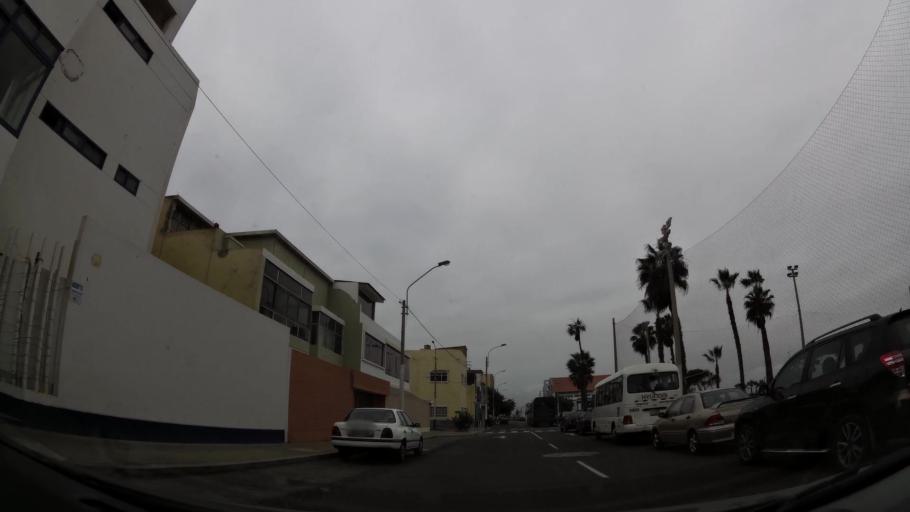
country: PE
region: Callao
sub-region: Callao
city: Callao
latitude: -12.0740
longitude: -77.1630
